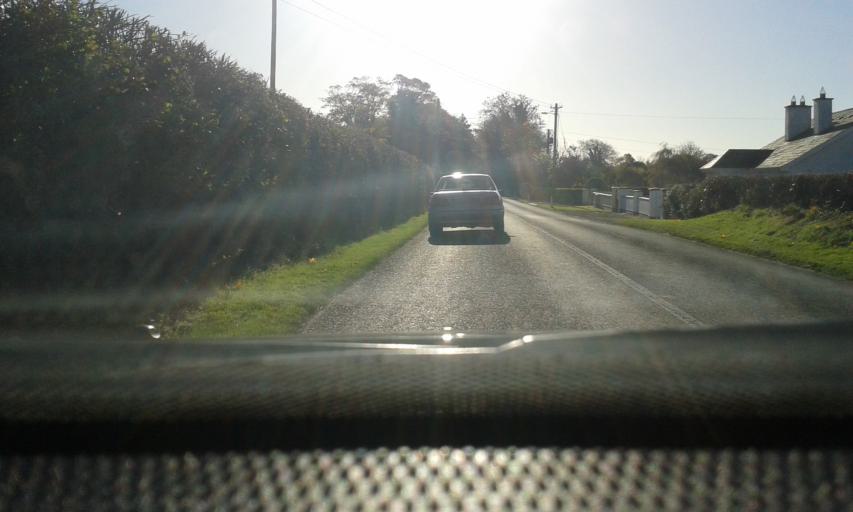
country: IE
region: Leinster
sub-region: Kildare
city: Rathangan
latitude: 53.2117
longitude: -6.9990
